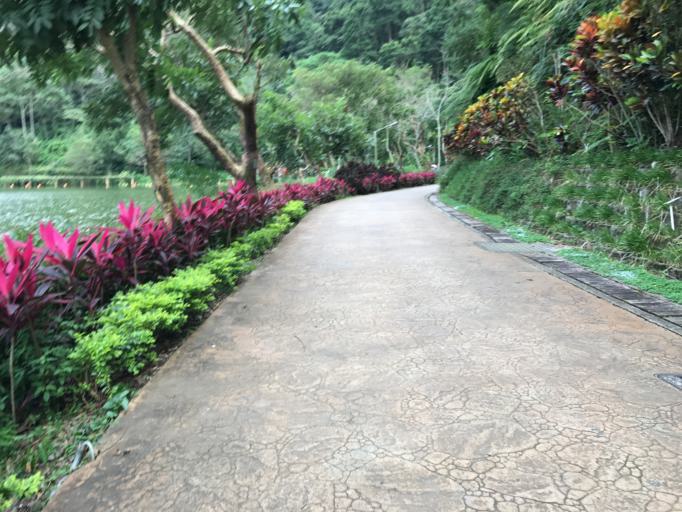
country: TW
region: Taiwan
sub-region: Nantou
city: Puli
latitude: 23.9588
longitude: 120.9950
